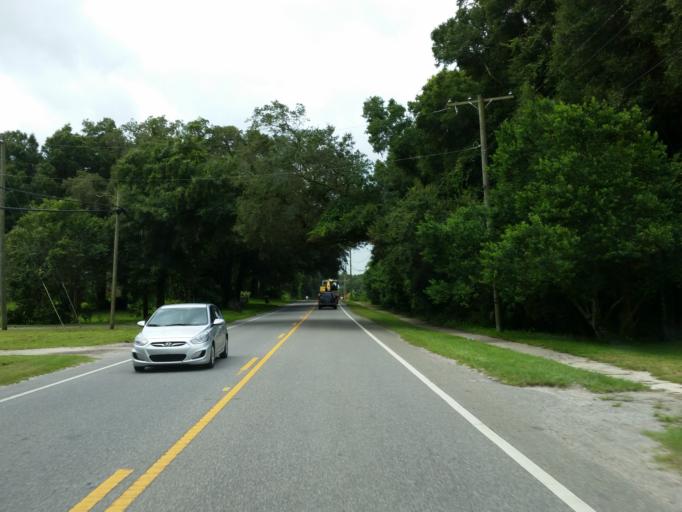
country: US
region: Florida
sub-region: Hillsborough County
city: Thonotosassa
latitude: 28.0266
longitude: -82.3026
